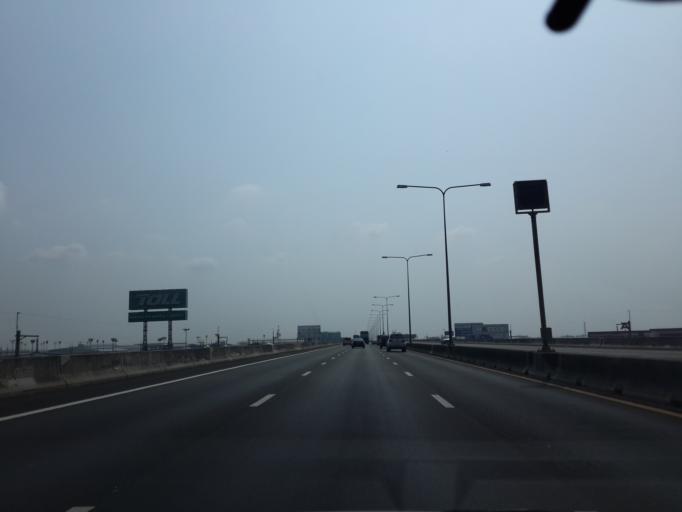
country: TH
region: Samut Prakan
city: Bang Bo District
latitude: 13.6004
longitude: 100.7897
